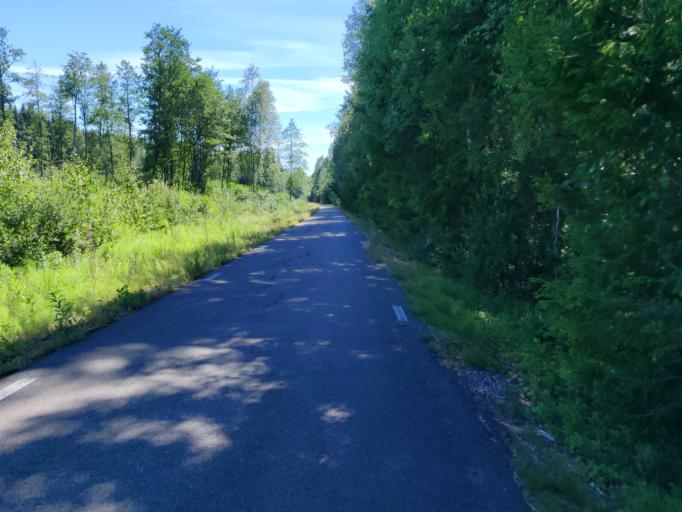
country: SE
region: Vaermland
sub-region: Hagfors Kommun
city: Hagfors
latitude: 59.9624
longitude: 13.5722
